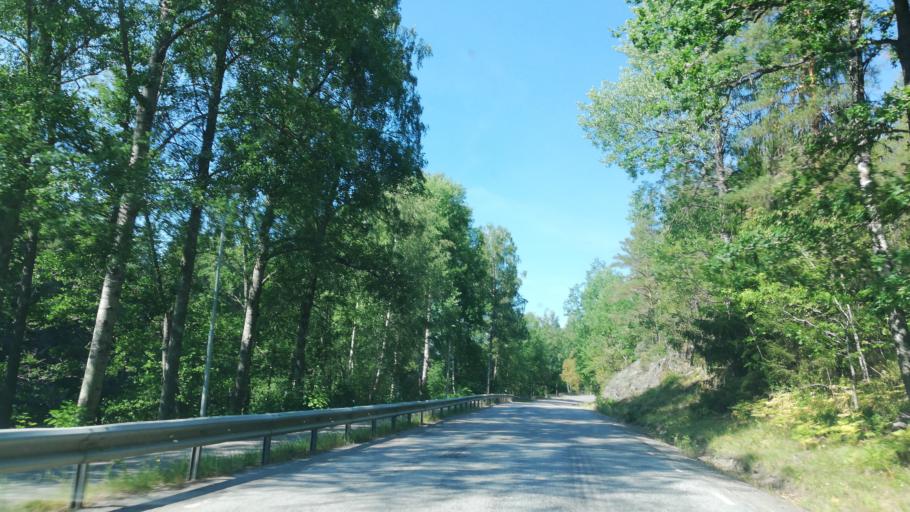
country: SE
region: OEstergoetland
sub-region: Finspangs Kommun
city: Finspang
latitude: 58.7209
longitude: 15.8322
